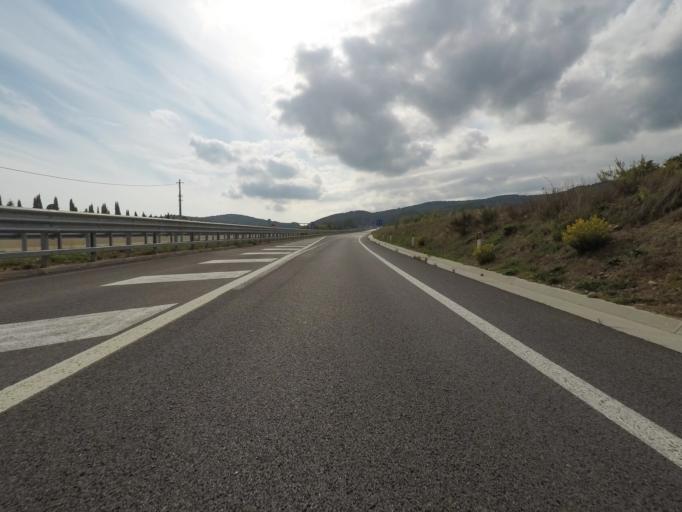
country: IT
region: Tuscany
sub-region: Provincia di Siena
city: Murlo
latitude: 43.1181
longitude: 11.2969
